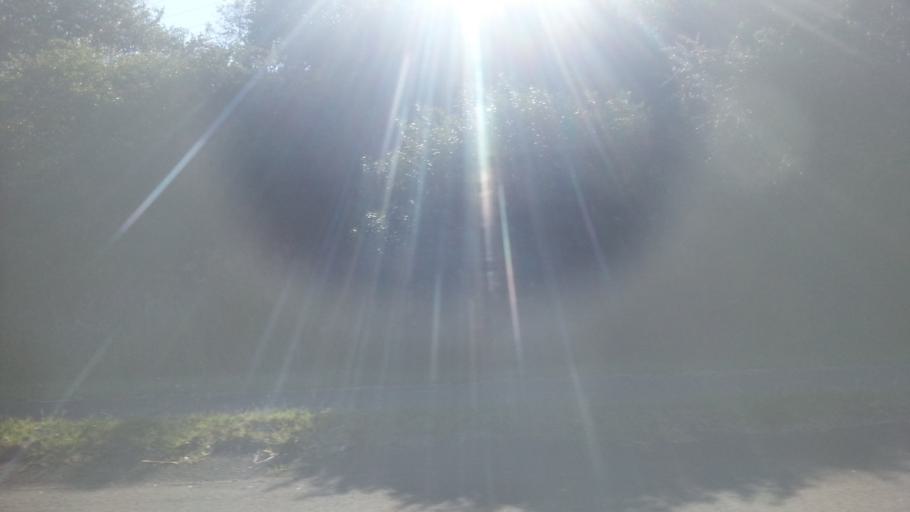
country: AU
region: New South Wales
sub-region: Wollongong
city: Berkeley
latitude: -34.4690
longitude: 150.8523
